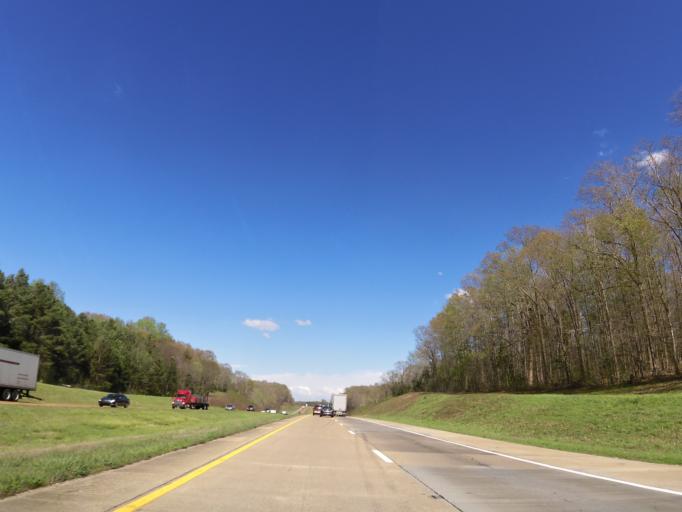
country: US
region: Tennessee
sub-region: Gibson County
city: Medina
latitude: 35.7250
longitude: -88.6116
